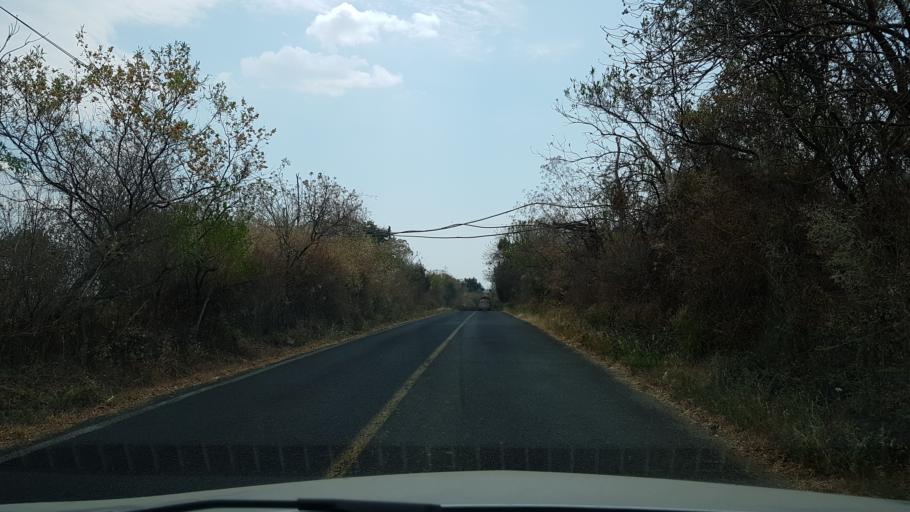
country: MX
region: Puebla
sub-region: Tochimilco
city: San Antonio Alpanocan
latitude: 18.8361
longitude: -98.7221
